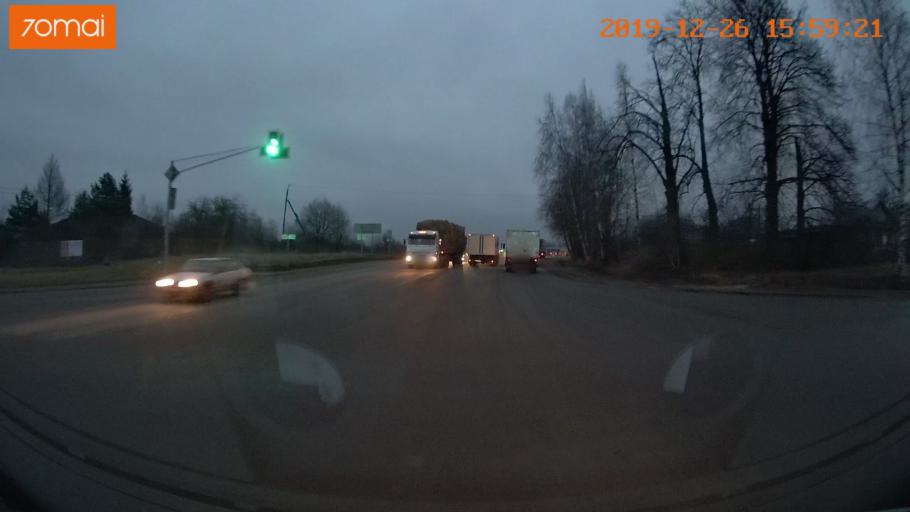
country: RU
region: Jaroslavl
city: Rybinsk
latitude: 58.0322
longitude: 38.8036
